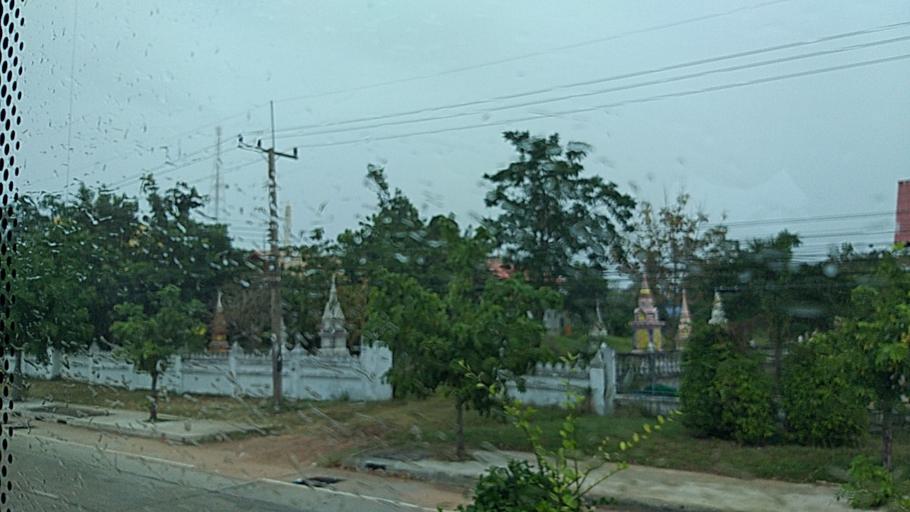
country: TH
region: Maha Sarakham
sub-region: Amphoe Borabue
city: Borabue
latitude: 16.0370
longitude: 103.1246
